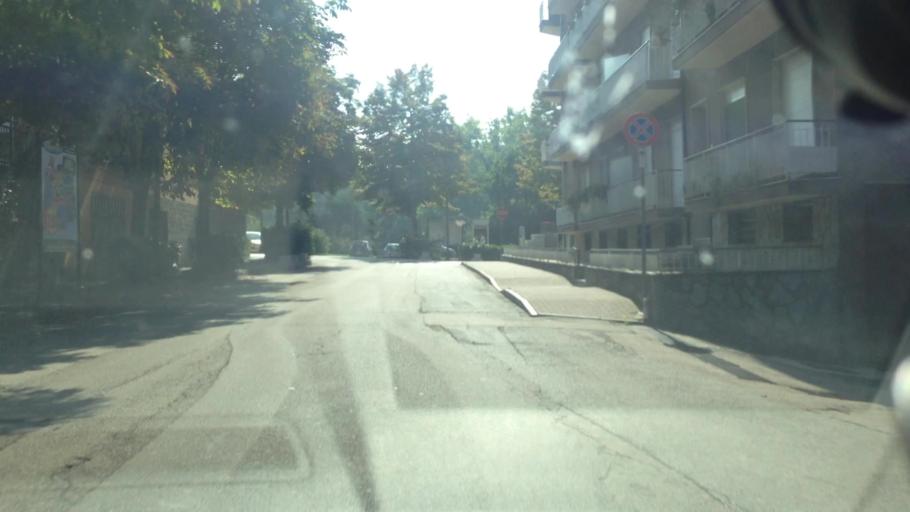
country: IT
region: Piedmont
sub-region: Provincia di Asti
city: Asti
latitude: 44.9038
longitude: 8.1920
